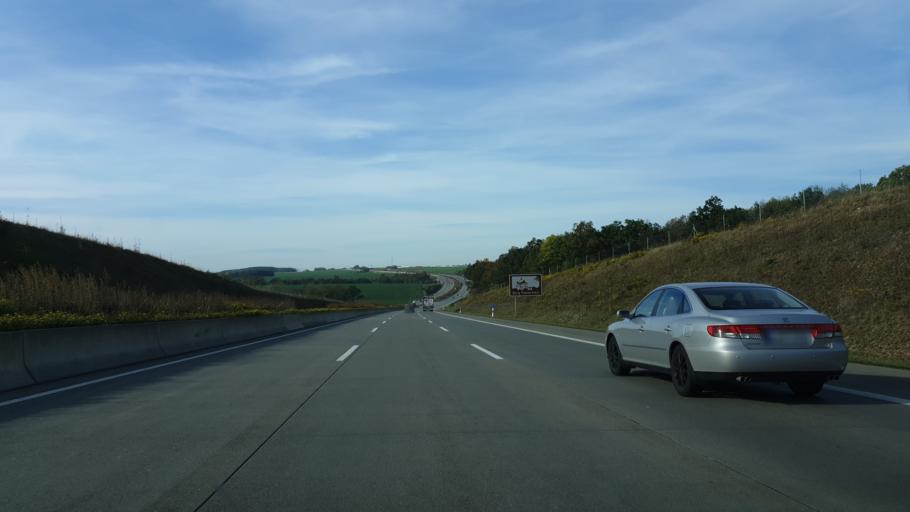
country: DE
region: Thuringia
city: Nobdenitz
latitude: 50.8654
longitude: 12.2765
